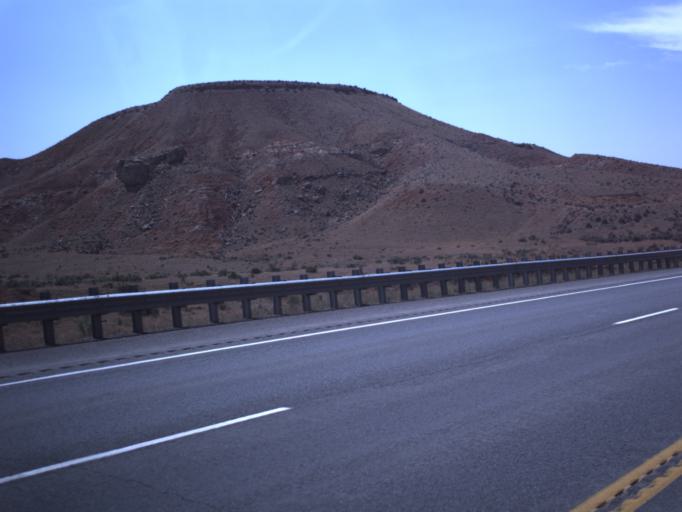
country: US
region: Utah
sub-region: Uintah County
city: Maeser
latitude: 40.3540
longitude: -109.6193
